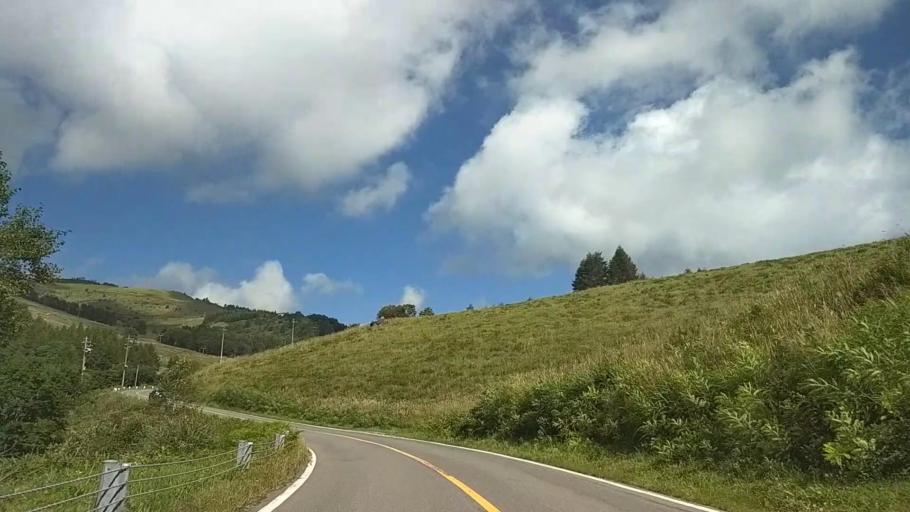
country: JP
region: Nagano
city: Suwa
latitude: 36.0992
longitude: 138.2151
